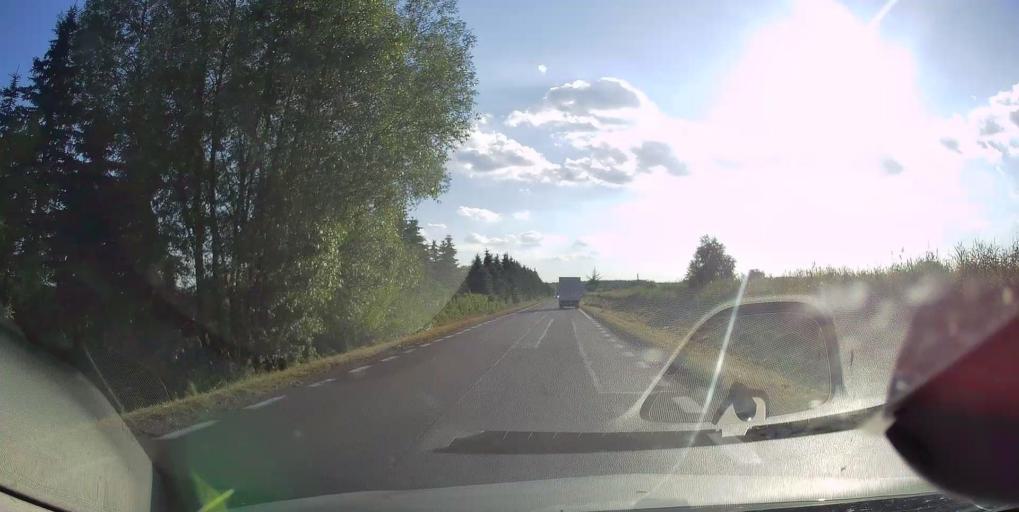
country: PL
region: Lodz Voivodeship
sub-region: Powiat rawski
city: Biala Rawska
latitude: 51.8036
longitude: 20.4607
